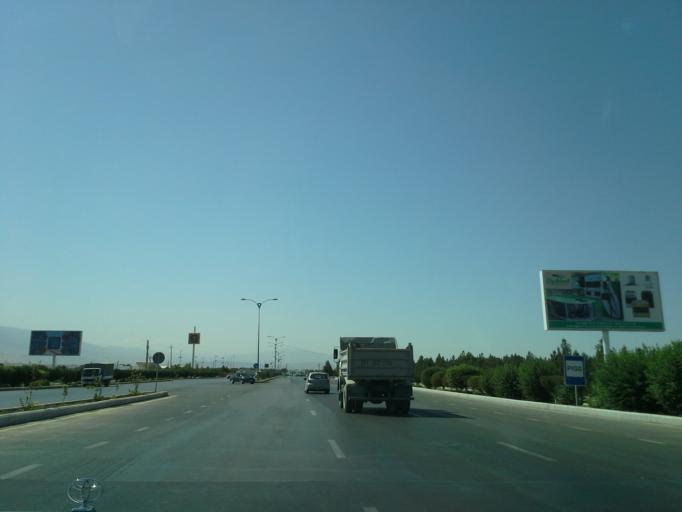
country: TM
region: Ahal
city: Annau
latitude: 37.9068
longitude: 58.5220
